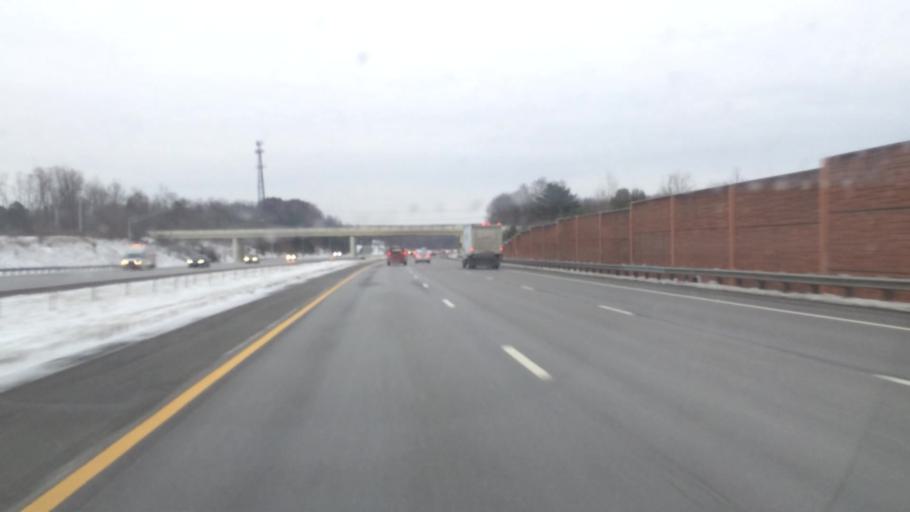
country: US
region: Ohio
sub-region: Medina County
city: Brunswick
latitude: 41.2285
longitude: -81.7950
